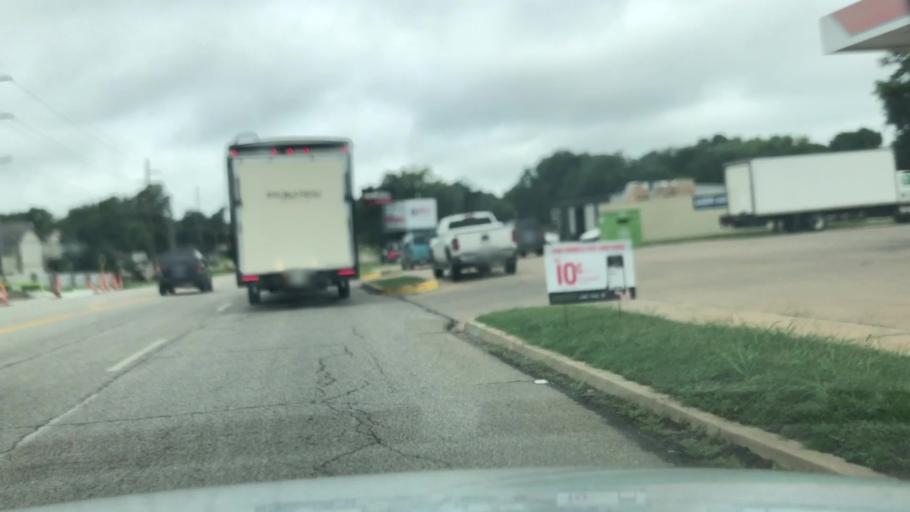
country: US
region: Oklahoma
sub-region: Washington County
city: Bartlesville
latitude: 36.7281
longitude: -95.9176
